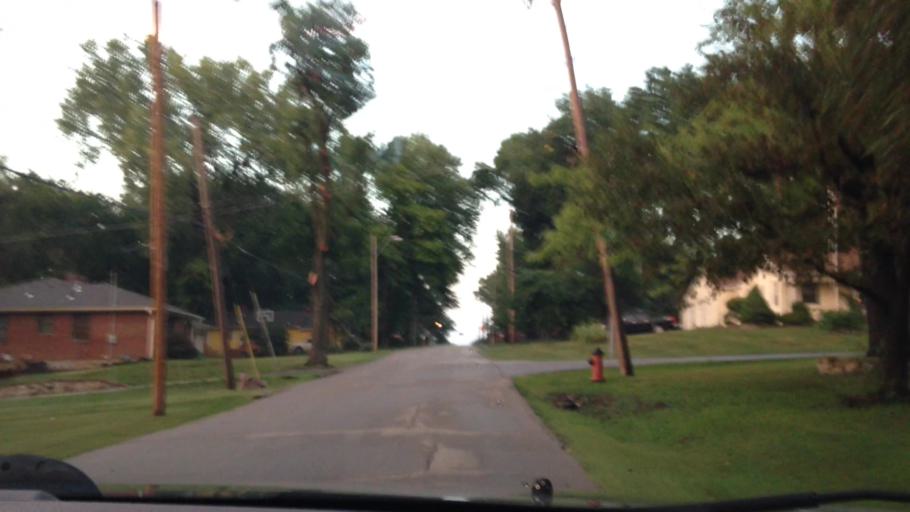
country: US
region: Missouri
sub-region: Clay County
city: Gladstone
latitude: 39.2434
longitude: -94.5806
